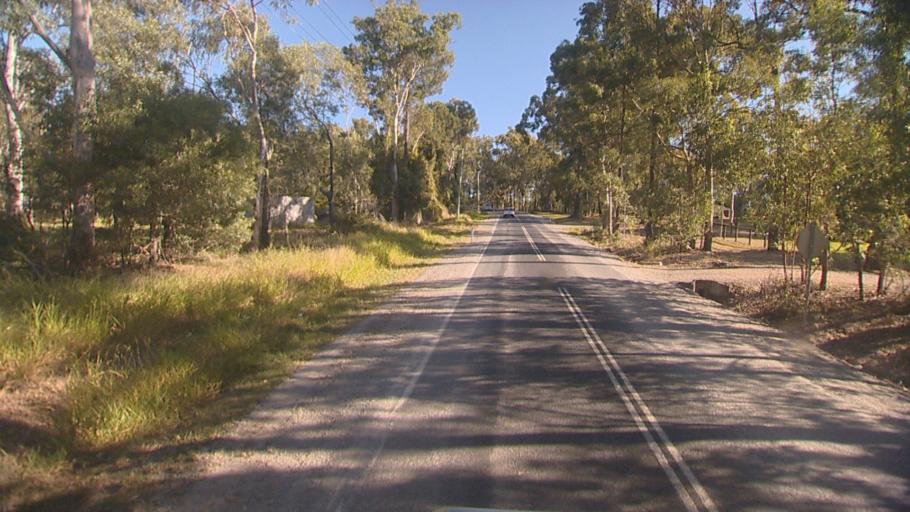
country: AU
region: Queensland
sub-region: Logan
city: Waterford West
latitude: -27.7410
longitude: 153.1448
